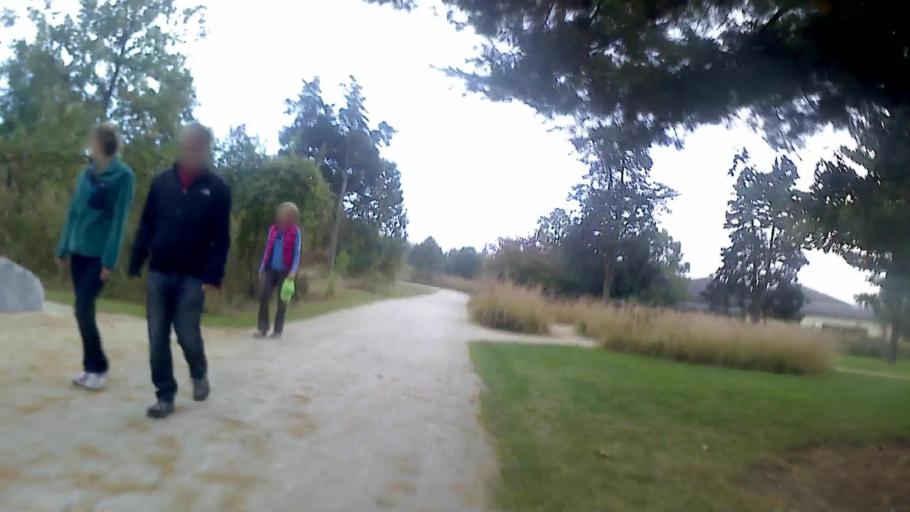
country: US
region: Illinois
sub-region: DuPage County
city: Lisle
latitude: 41.8203
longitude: -88.1118
